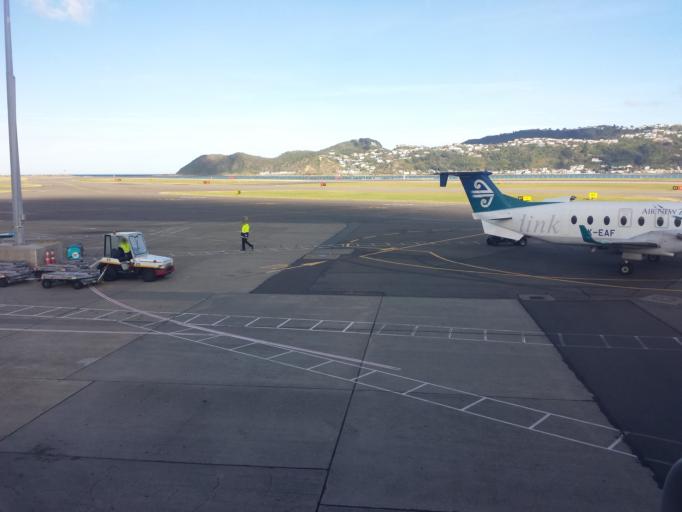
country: NZ
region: Wellington
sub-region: Wellington City
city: Wellington
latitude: -41.3298
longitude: 174.8097
